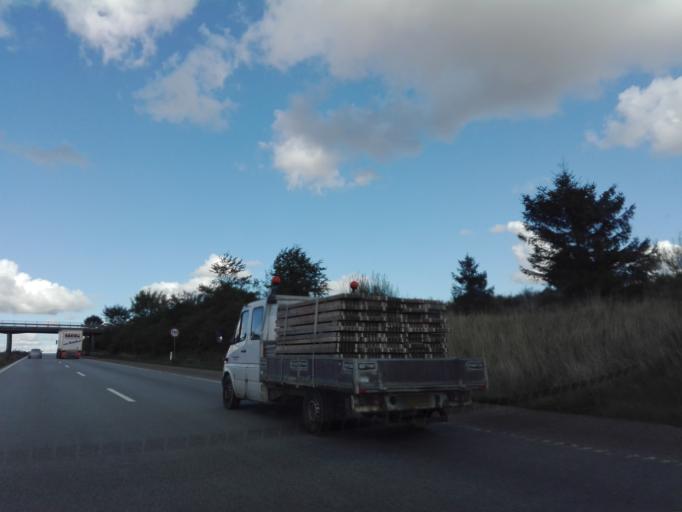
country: DK
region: Central Jutland
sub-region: Randers Kommune
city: Randers
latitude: 56.4839
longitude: 9.9808
